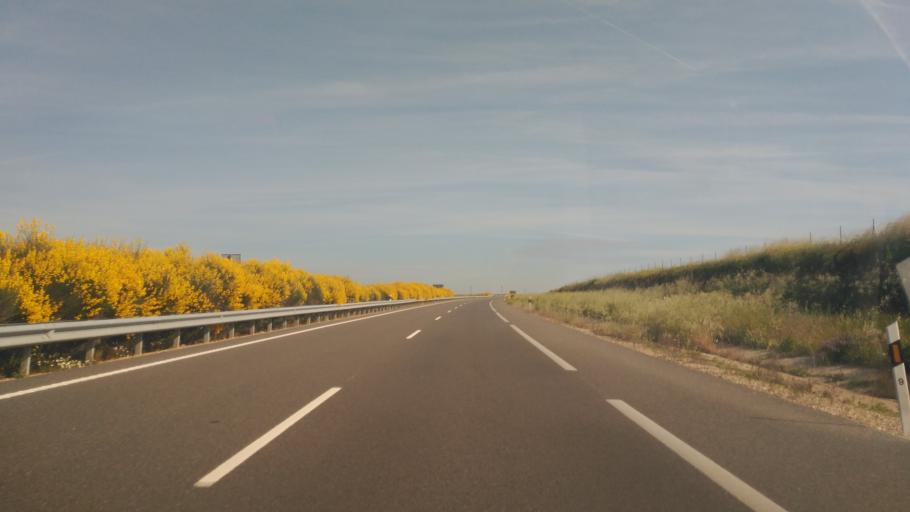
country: ES
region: Castille and Leon
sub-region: Provincia de Salamanca
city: Calzada de Valdunciel
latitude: 41.0967
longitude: -5.6961
